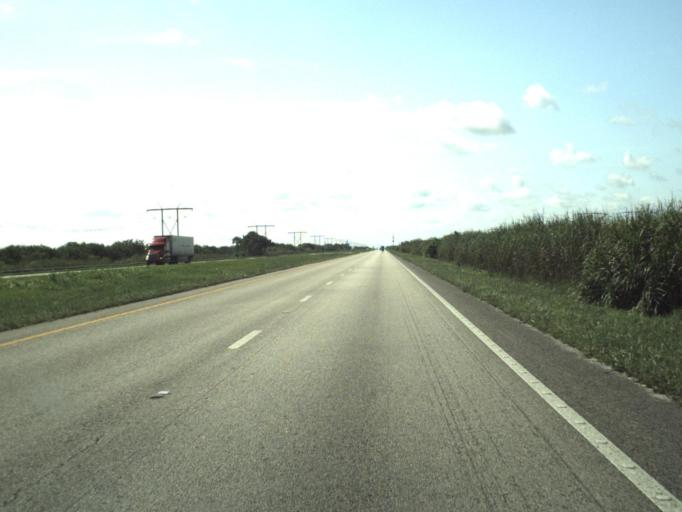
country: US
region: Florida
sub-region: Broward County
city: Weston
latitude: 26.2891
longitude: -80.5027
